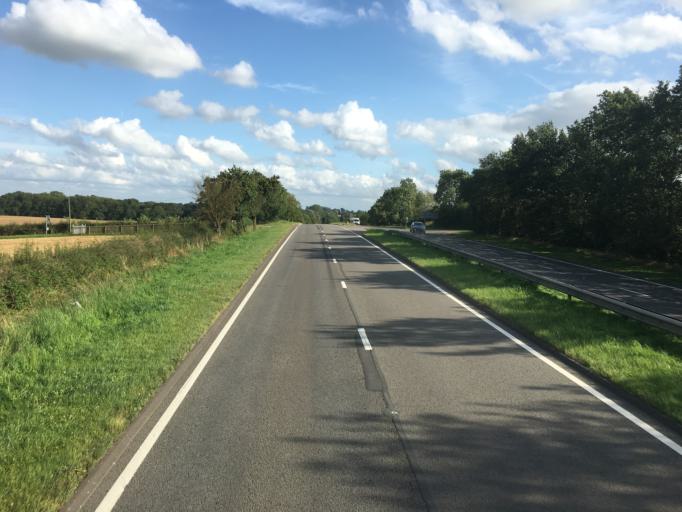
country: GB
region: England
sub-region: Leicestershire
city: Lutterworth
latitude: 52.4405
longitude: -1.2423
